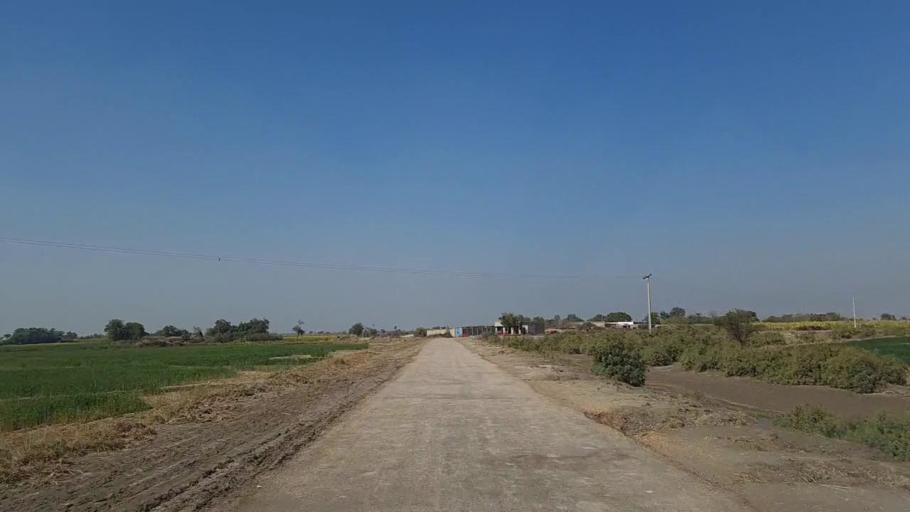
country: PK
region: Sindh
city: Nawabshah
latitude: 26.3379
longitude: 68.4267
